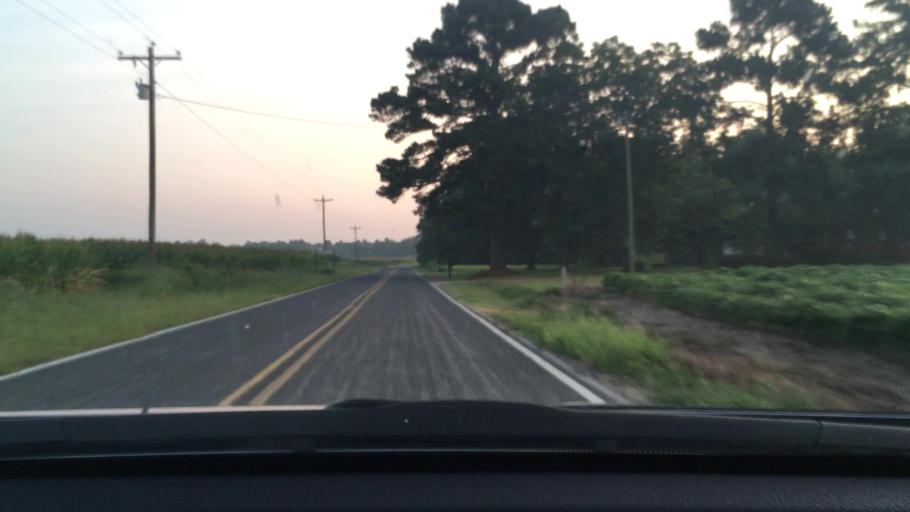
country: US
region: South Carolina
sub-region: Lee County
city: Bishopville
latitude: 34.1796
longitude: -80.1435
